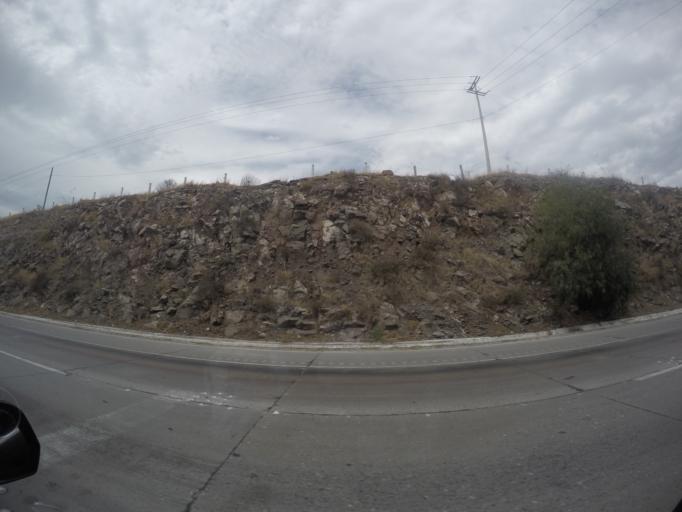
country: MX
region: Queretaro
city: San Juan del Rio
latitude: 20.3642
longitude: -99.9752
